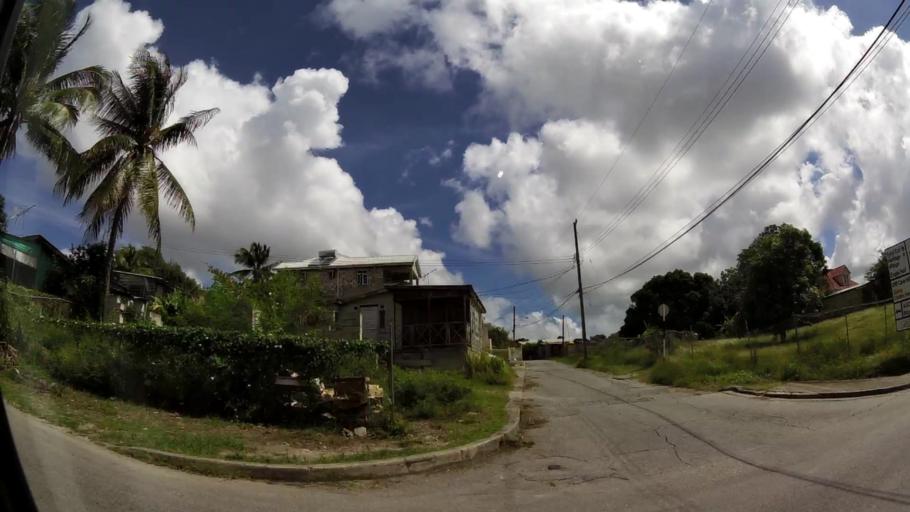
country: BB
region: Saint Michael
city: Bridgetown
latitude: 13.1367
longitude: -59.6240
